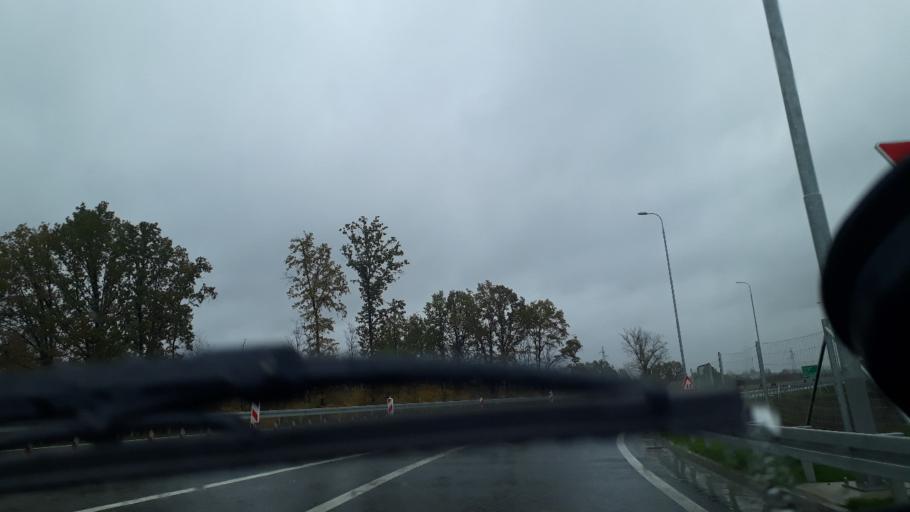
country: BA
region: Republika Srpska
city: Prnjavor
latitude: 44.8506
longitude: 17.6789
